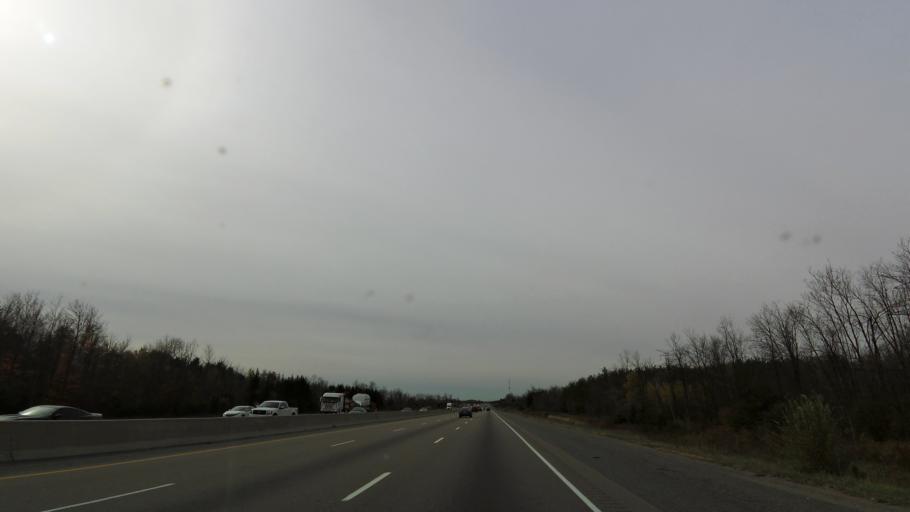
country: CA
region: Ontario
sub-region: Halton
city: Milton
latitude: 43.4700
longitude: -80.0692
